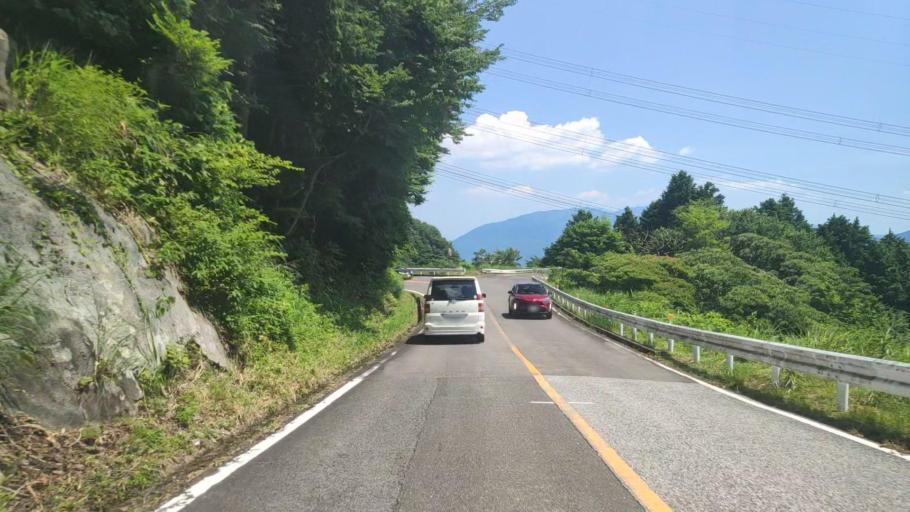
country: JP
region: Gifu
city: Tarui
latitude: 35.3846
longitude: 136.4446
